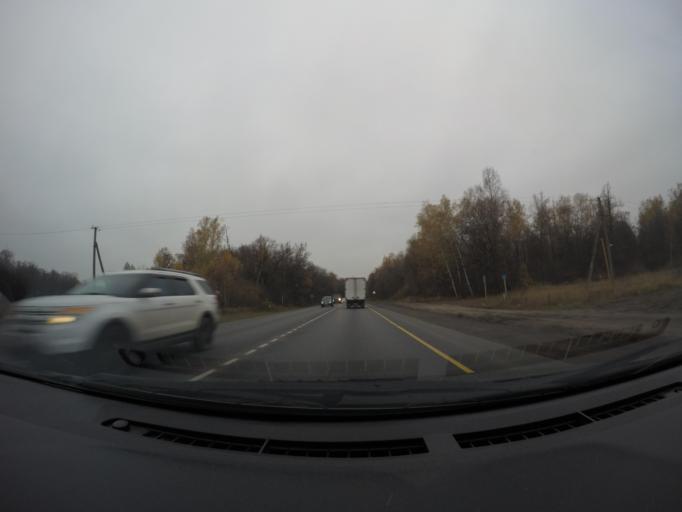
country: RU
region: Moskovskaya
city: Bronnitsy
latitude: 55.3984
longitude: 38.2248
